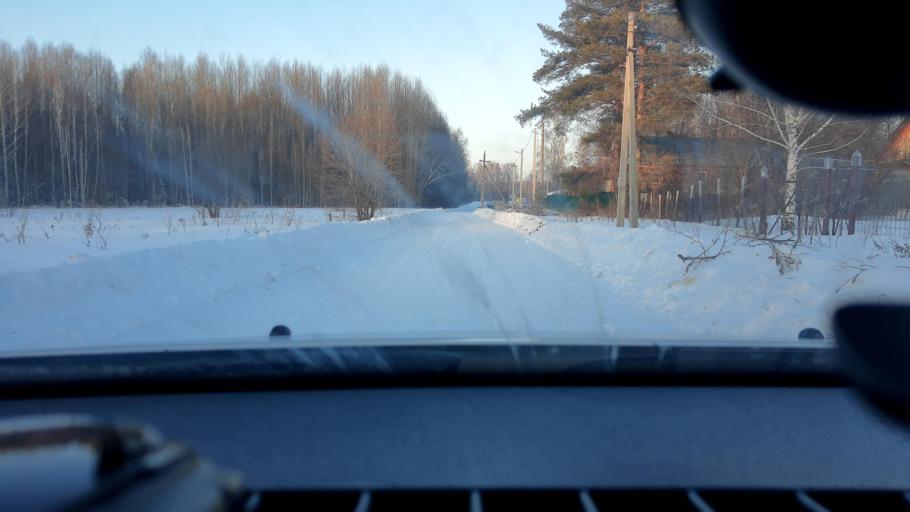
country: RU
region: Bashkortostan
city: Kudeyevskiy
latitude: 54.7991
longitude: 56.6755
